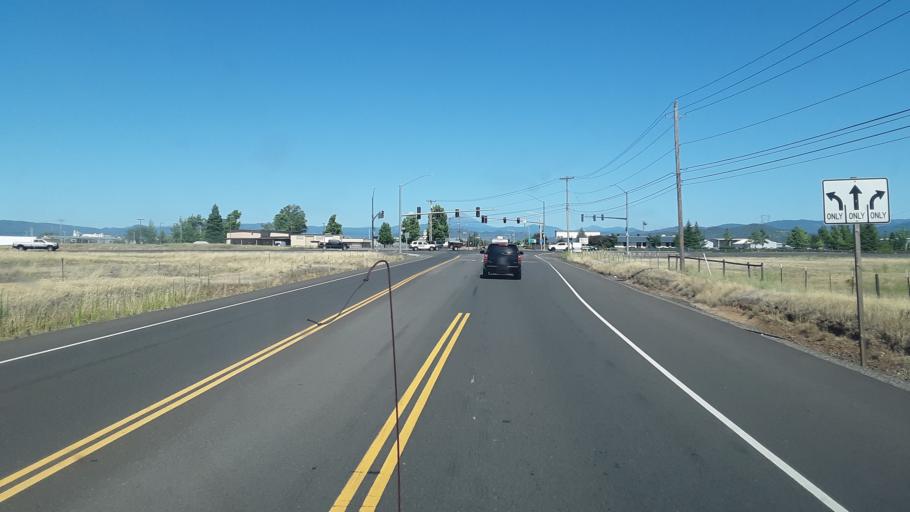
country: US
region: Oregon
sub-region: Jackson County
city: White City
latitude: 42.4273
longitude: -122.8878
